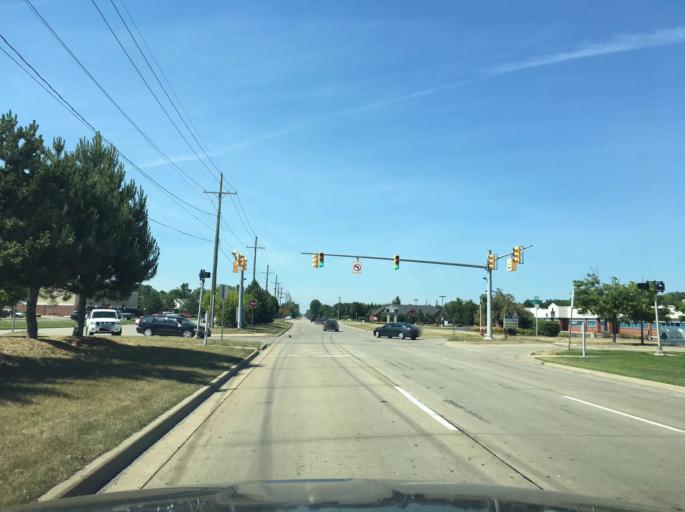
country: US
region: Michigan
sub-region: Macomb County
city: Utica
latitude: 42.6305
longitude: -82.9931
